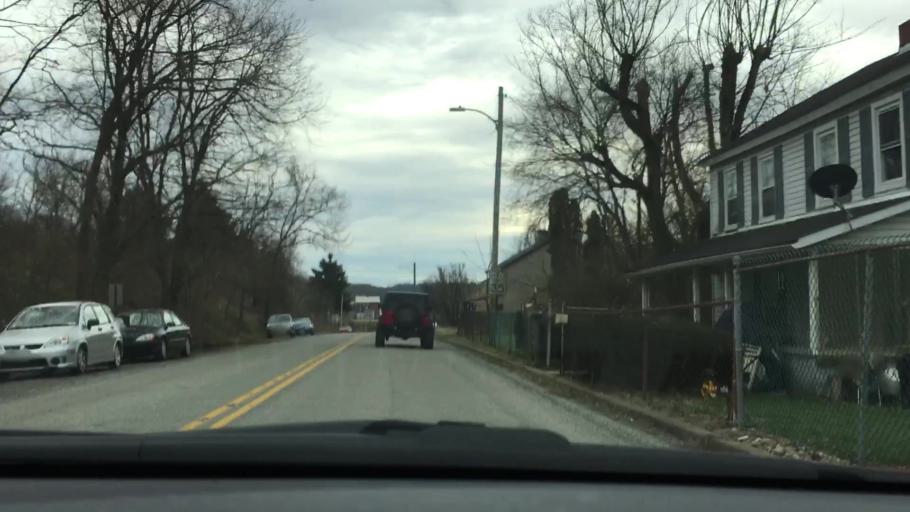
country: US
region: Pennsylvania
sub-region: Washington County
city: Midland
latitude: 40.2602
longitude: -80.2195
